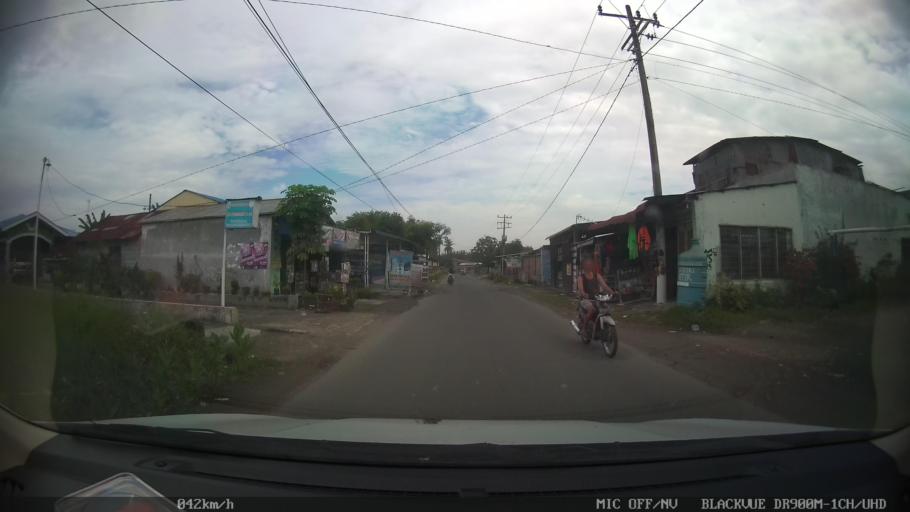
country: ID
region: North Sumatra
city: Sunggal
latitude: 3.6473
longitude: 98.5941
